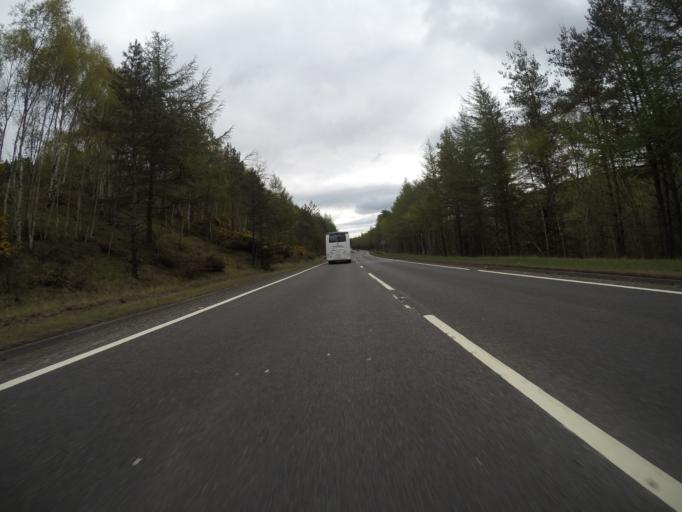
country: GB
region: Scotland
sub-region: Perth and Kinross
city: Aberfeldy
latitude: 56.7757
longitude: -3.9838
